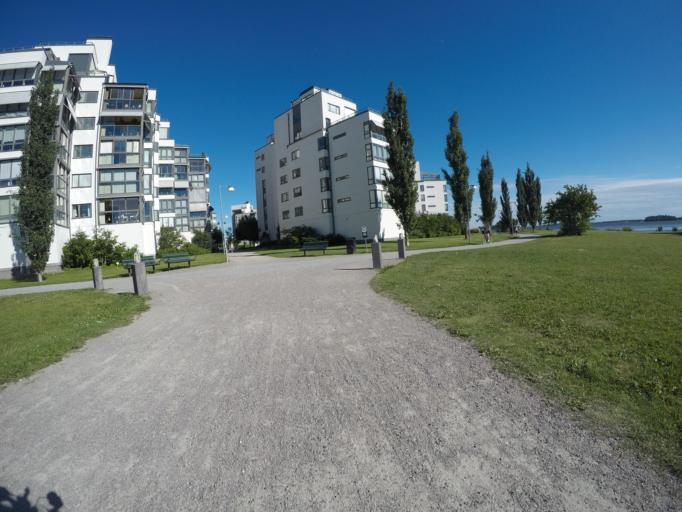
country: SE
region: Vaestmanland
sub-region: Vasteras
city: Vasteras
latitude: 59.6036
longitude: 16.5552
